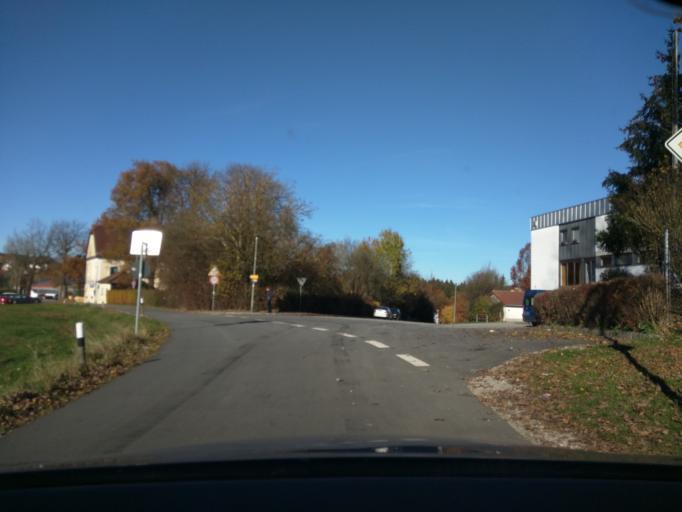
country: DE
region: Bavaria
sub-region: Lower Bavaria
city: Salzweg
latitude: 48.5834
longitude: 13.4909
